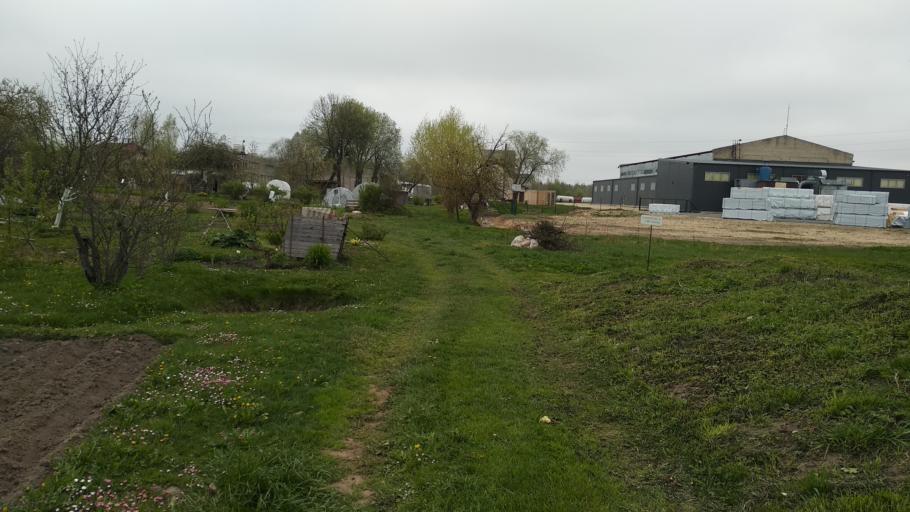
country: LV
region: Malpils
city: Malpils
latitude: 57.0144
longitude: 24.9589
